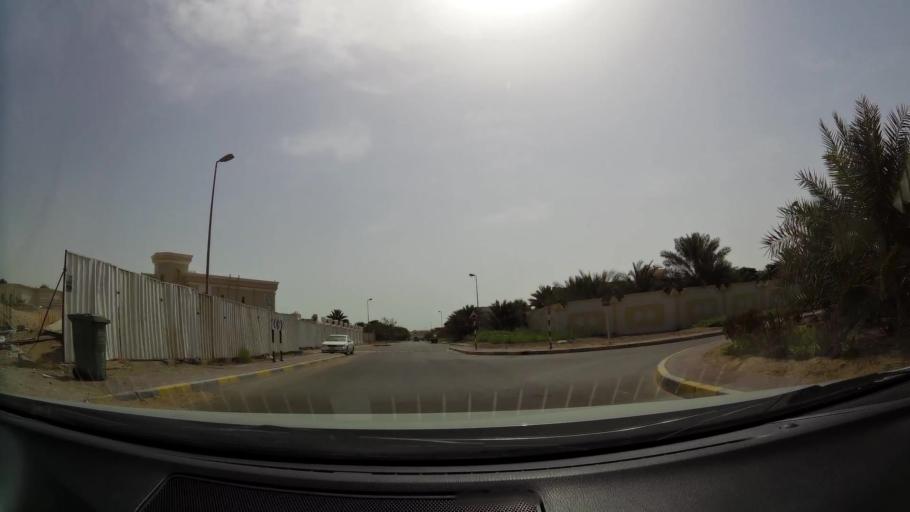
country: AE
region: Abu Dhabi
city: Al Ain
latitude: 24.1578
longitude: 55.6803
